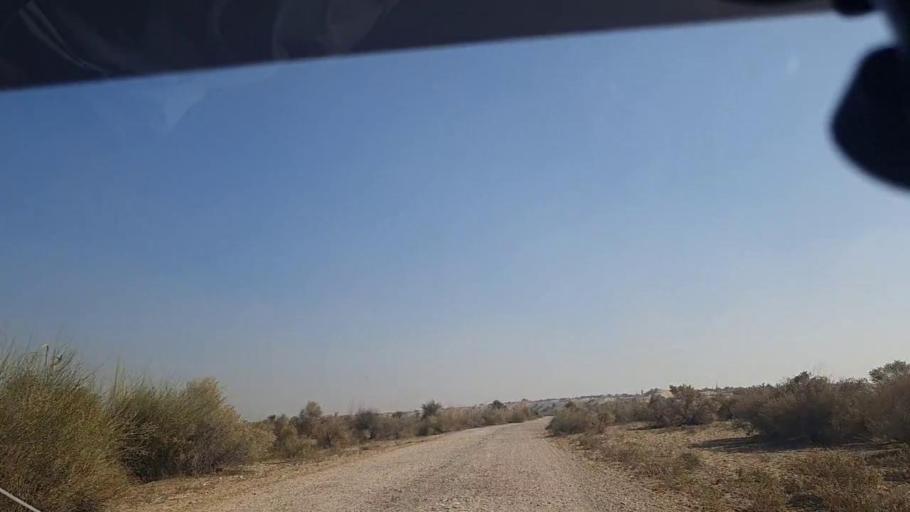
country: PK
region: Sindh
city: Khanpur
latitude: 27.5618
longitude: 69.3235
